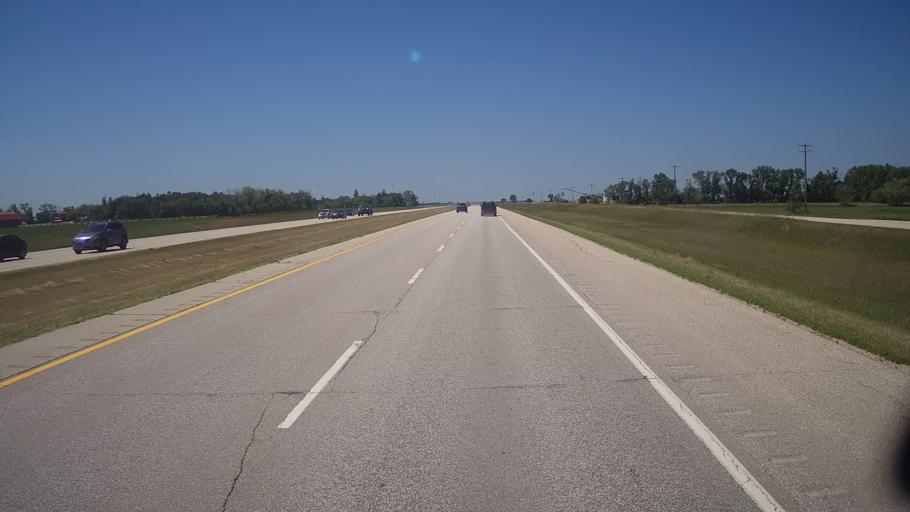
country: CA
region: Manitoba
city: Stonewall
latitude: 49.9900
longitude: -97.2660
